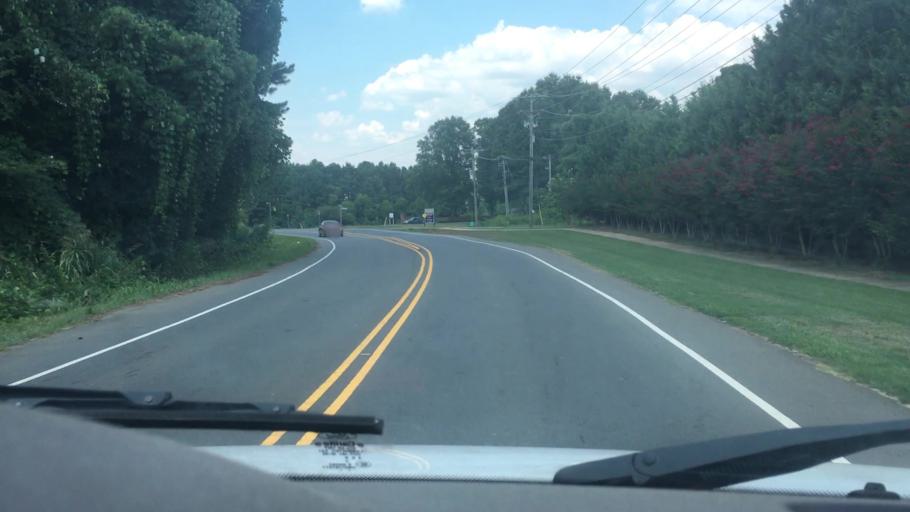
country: US
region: North Carolina
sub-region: Mecklenburg County
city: Huntersville
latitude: 35.3985
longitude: -80.8705
